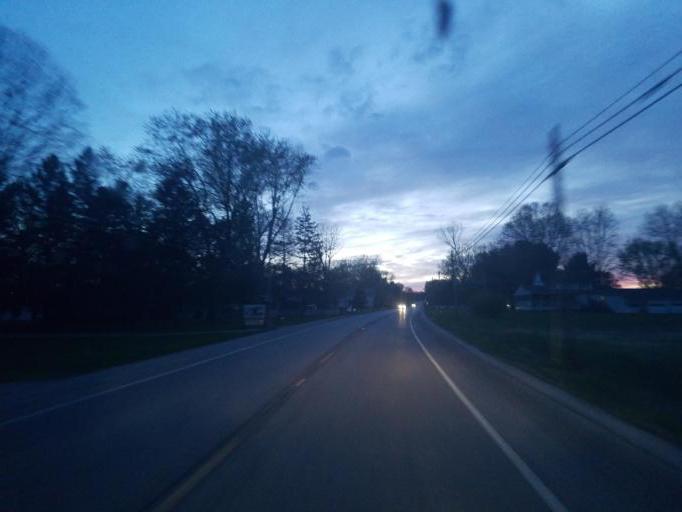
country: US
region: Ohio
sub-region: Wayne County
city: Apple Creek
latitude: 40.7568
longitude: -81.8706
